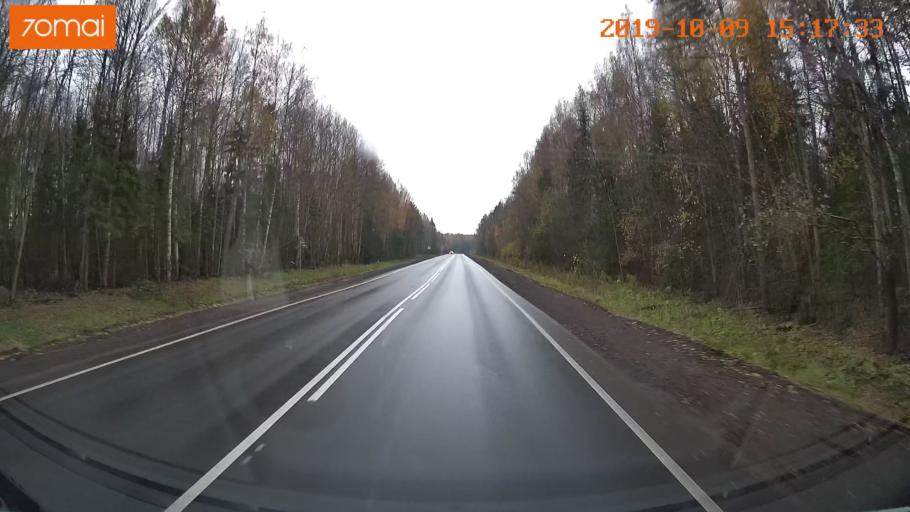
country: RU
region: Kostroma
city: Susanino
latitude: 58.0968
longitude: 41.5823
